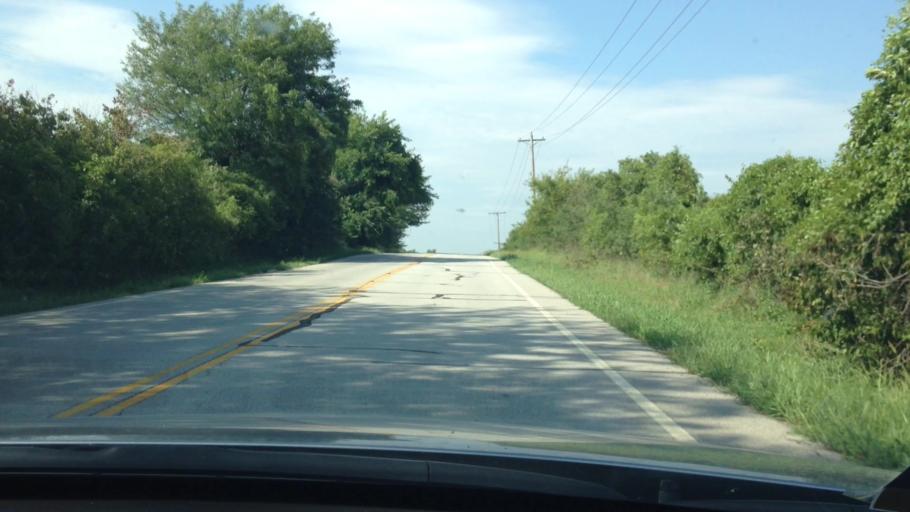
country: US
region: Missouri
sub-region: Platte County
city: Platte City
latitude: 39.3128
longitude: -94.7611
